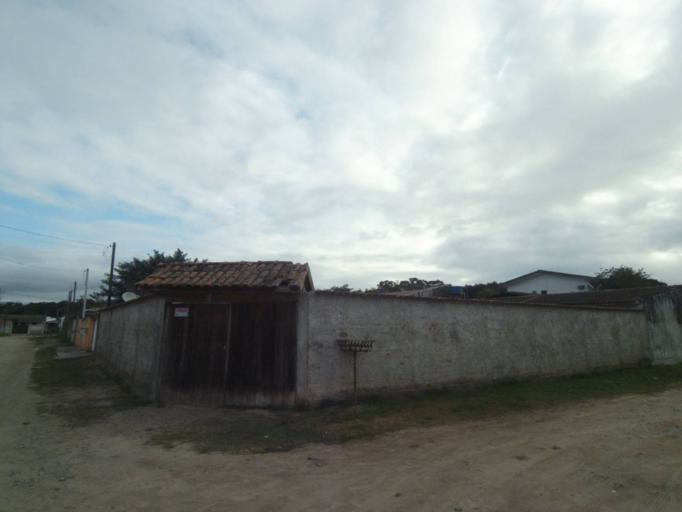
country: BR
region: Parana
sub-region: Paranagua
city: Paranagua
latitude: -25.5334
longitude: -48.5492
